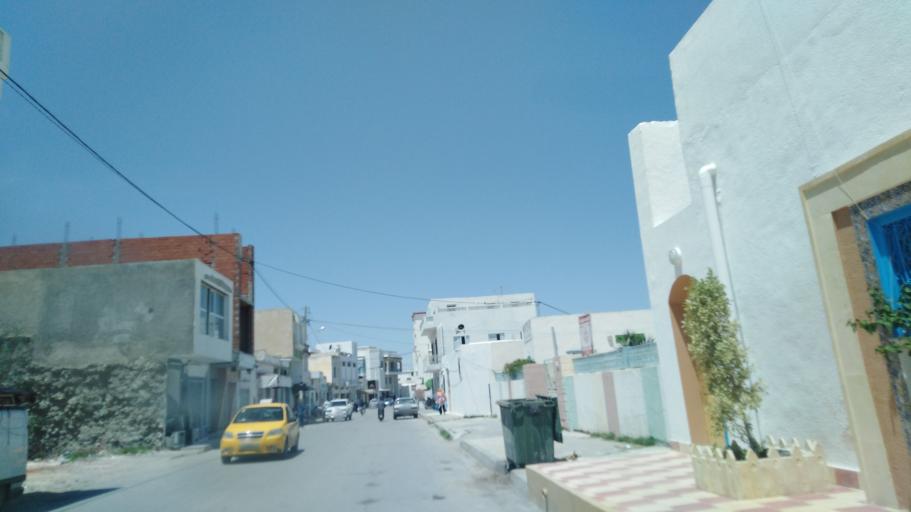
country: TN
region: Al Mahdiyah
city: Ksour Essaf
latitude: 35.4168
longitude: 10.9944
